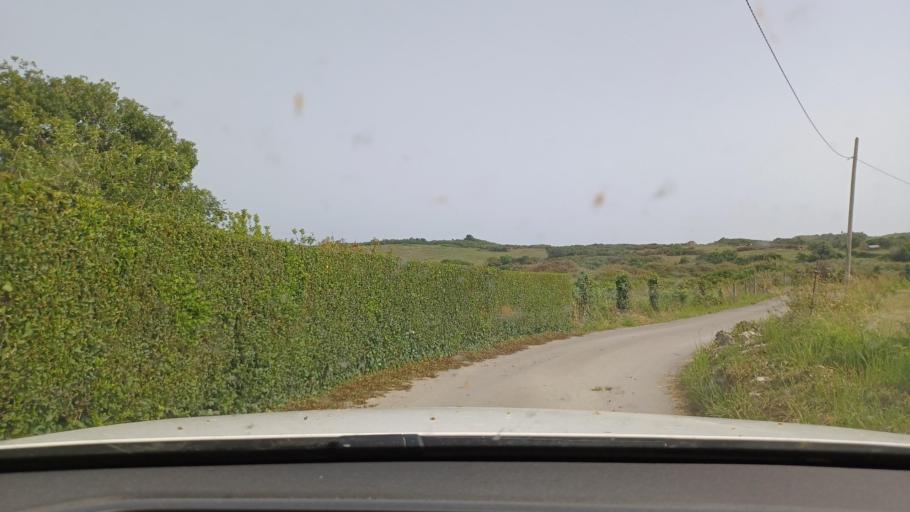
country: ES
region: Asturias
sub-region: Province of Asturias
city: Ribadesella
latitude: 43.4575
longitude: -5.0332
